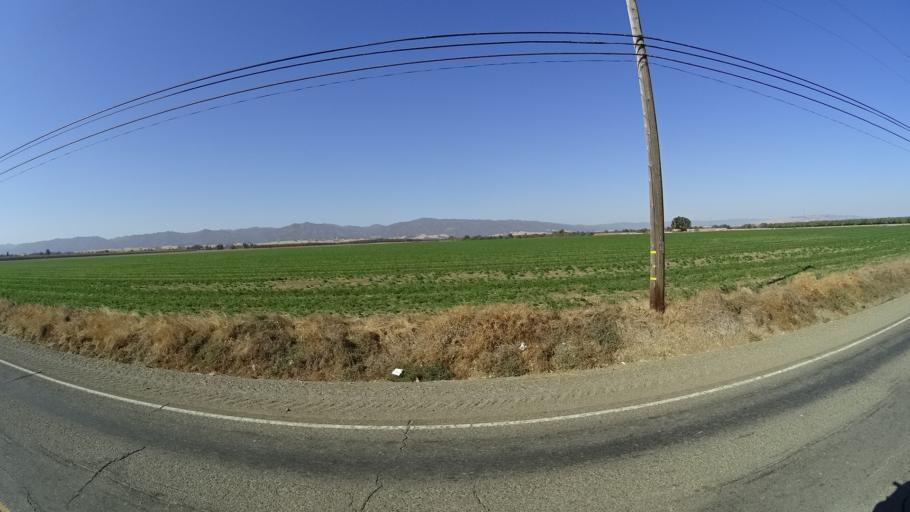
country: US
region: California
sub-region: Yolo County
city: Cottonwood
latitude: 38.6453
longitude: -121.9713
